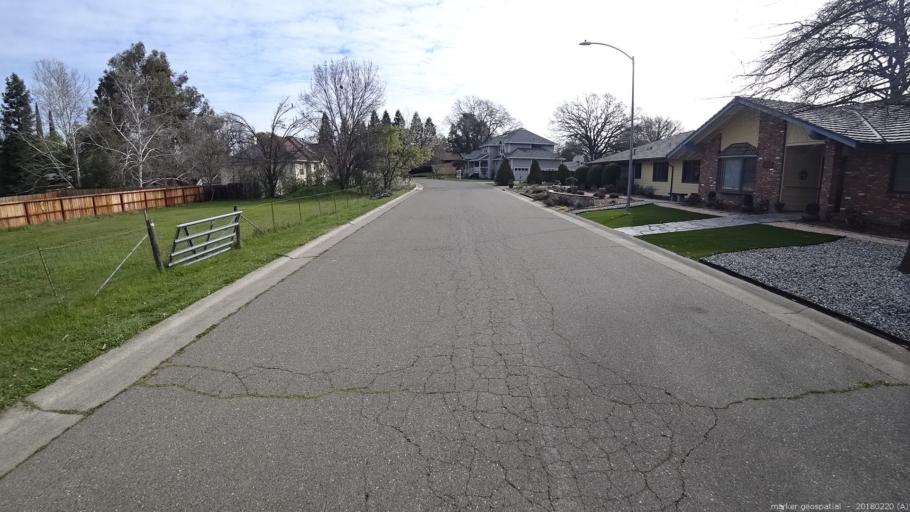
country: US
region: California
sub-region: Sacramento County
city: Orangevale
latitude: 38.6840
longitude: -121.2295
